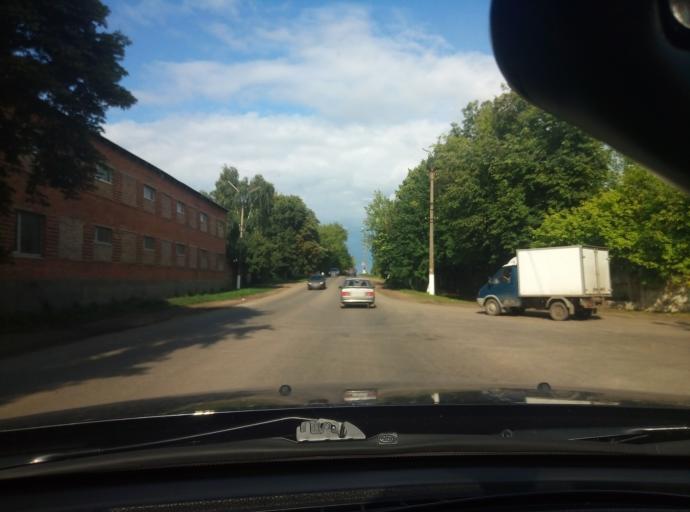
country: RU
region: Tula
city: Donskoy
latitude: 53.9679
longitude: 38.3433
